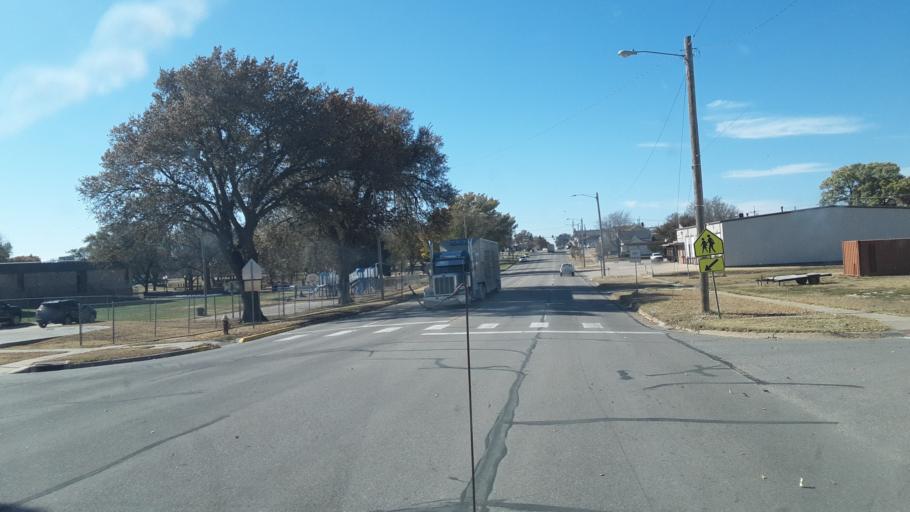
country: US
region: Kansas
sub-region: Rice County
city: Lyons
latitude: 38.3478
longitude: -98.1983
